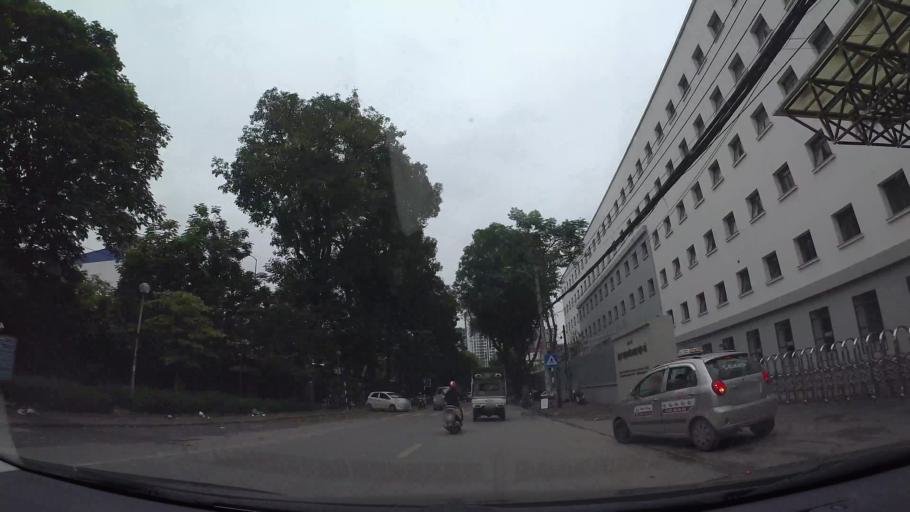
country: VN
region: Ha Noi
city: Hai BaTrung
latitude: 21.0158
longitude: 105.8623
